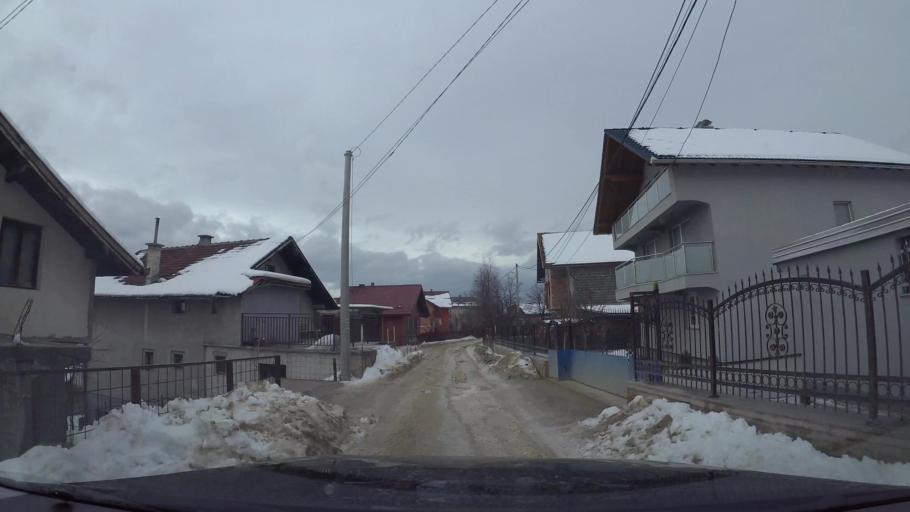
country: BA
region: Federation of Bosnia and Herzegovina
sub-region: Kanton Sarajevo
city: Sarajevo
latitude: 43.8664
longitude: 18.3274
